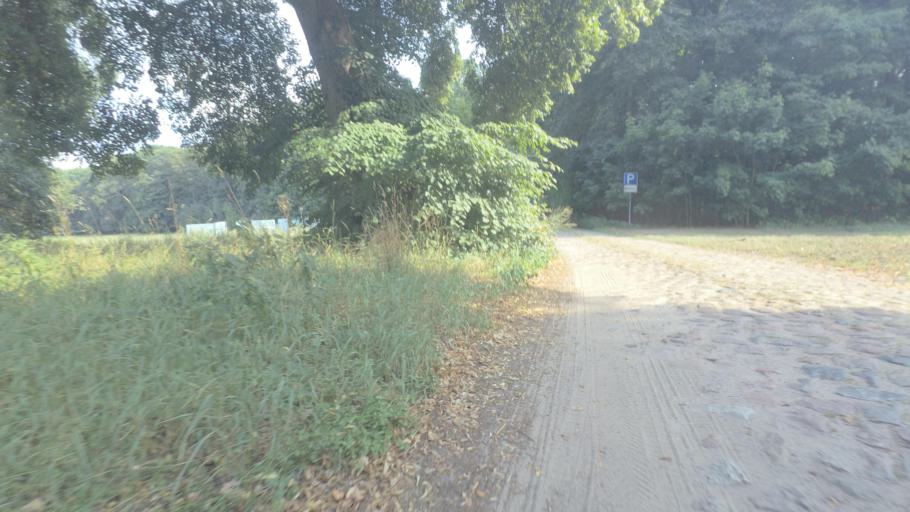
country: DE
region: Brandenburg
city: Wittstock
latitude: 53.2567
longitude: 12.4668
